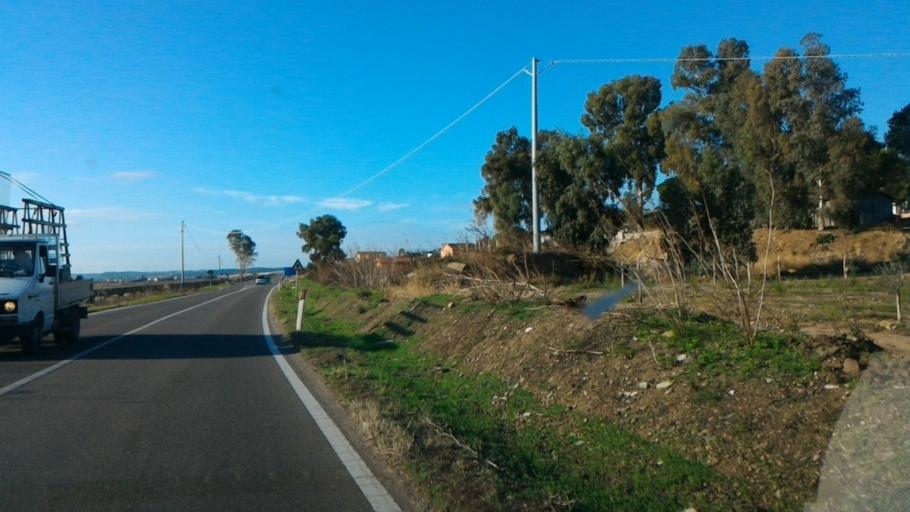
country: IT
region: Calabria
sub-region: Provincia di Crotone
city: Tronca
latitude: 39.1784
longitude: 17.1062
